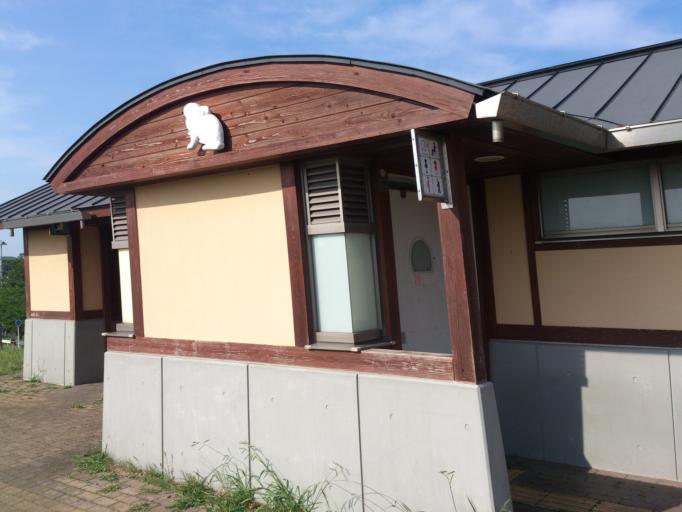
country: JP
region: Chiba
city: Matsudo
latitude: 35.7876
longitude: 139.8932
